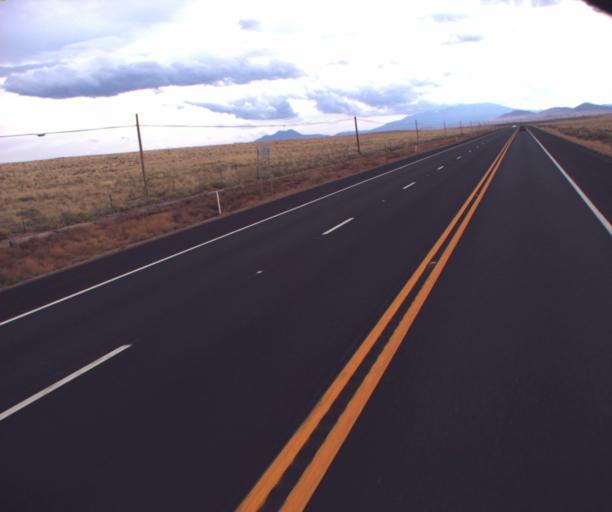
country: US
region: Arizona
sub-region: Coconino County
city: Tuba City
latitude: 35.6983
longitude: -111.5001
